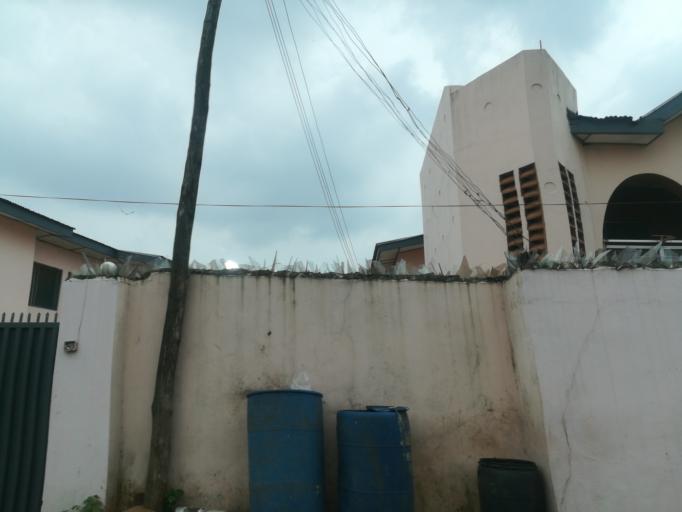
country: NG
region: Oyo
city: Ibadan
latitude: 7.4279
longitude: 3.9287
